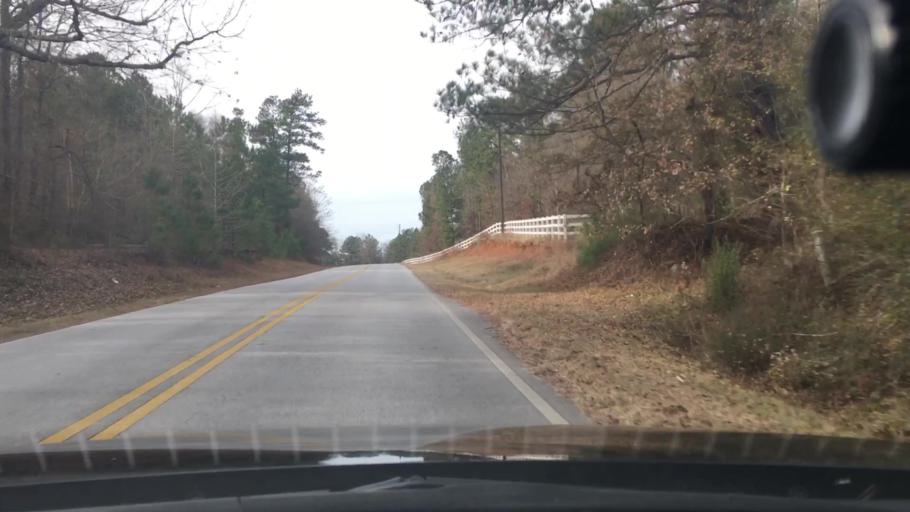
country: US
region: Georgia
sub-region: Spalding County
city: Experiment
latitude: 33.2813
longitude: -84.3982
